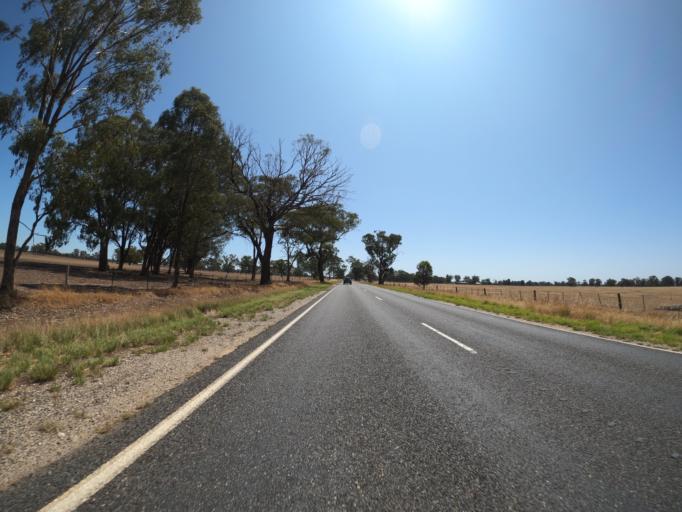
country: AU
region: New South Wales
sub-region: Corowa Shire
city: Corowa
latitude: -36.0751
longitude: 146.2480
